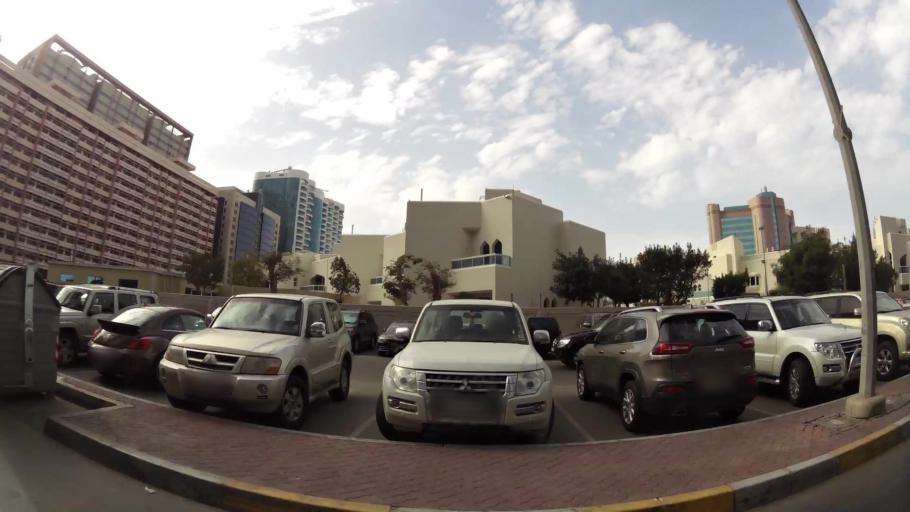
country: AE
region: Abu Dhabi
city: Abu Dhabi
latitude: 24.4712
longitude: 54.3440
